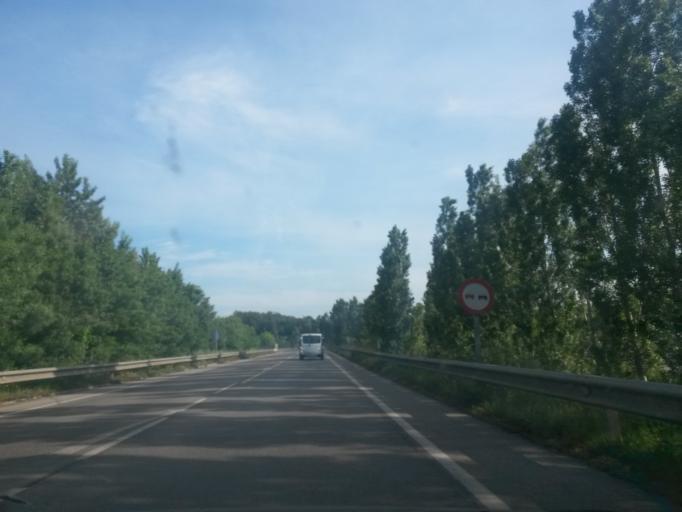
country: ES
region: Catalonia
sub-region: Provincia de Girona
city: la Cellera de Ter
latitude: 41.9733
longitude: 2.6240
